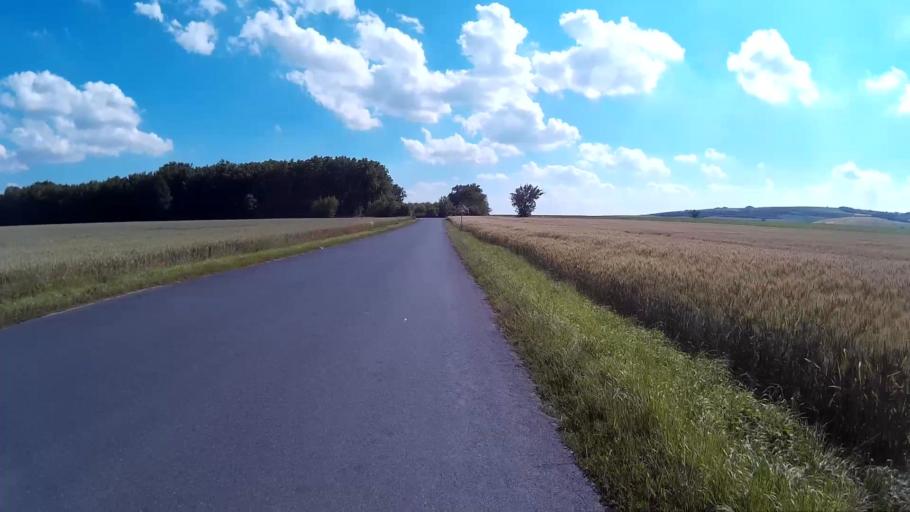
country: CZ
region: South Moravian
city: Menin
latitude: 49.0486
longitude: 16.6998
